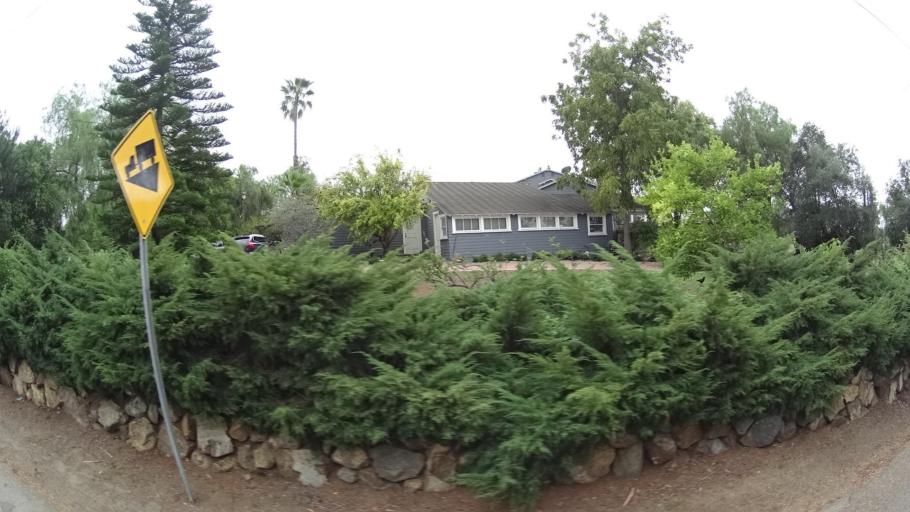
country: US
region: California
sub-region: San Diego County
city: Spring Valley
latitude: 32.7481
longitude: -116.9973
